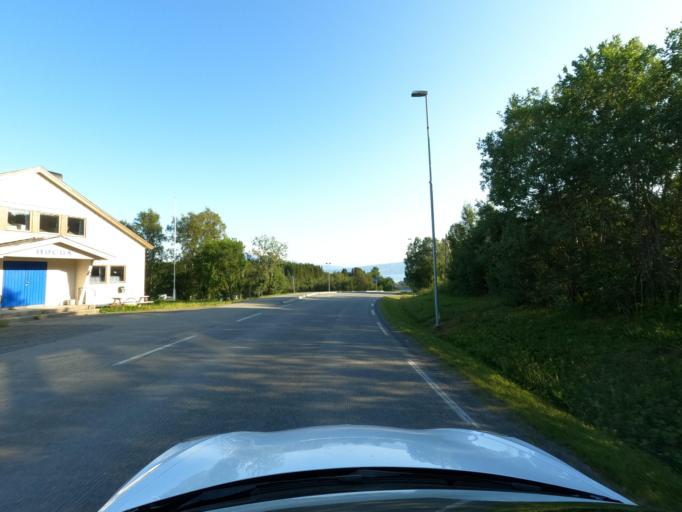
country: NO
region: Nordland
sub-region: Evenes
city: Randa
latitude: 68.4890
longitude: 16.9000
